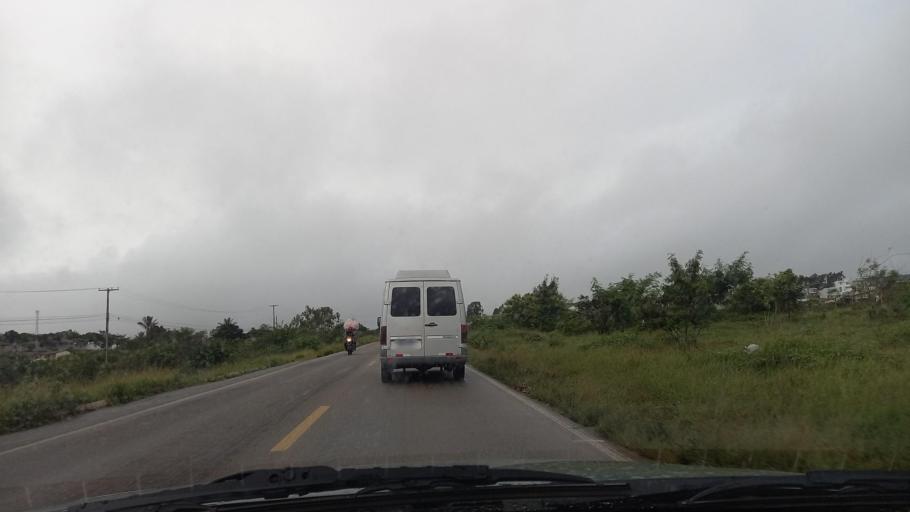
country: BR
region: Pernambuco
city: Garanhuns
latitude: -8.8637
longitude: -36.5101
